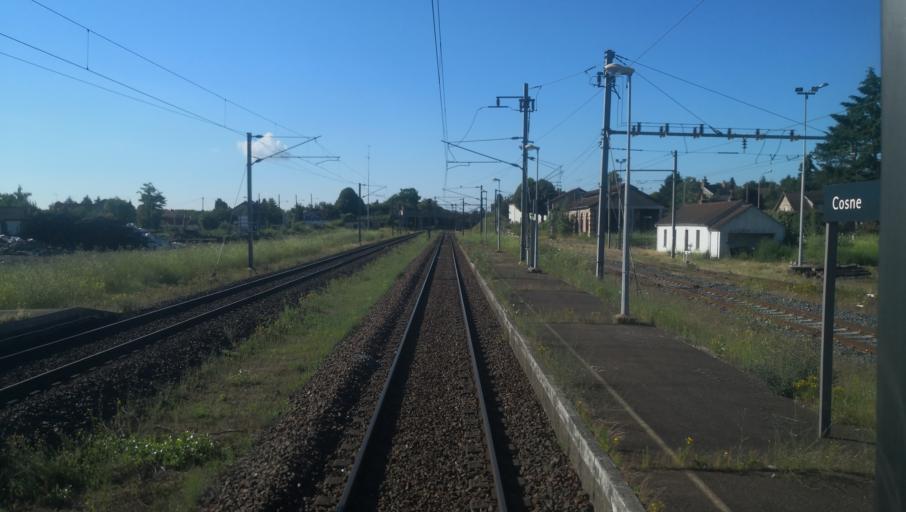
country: FR
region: Bourgogne
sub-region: Departement de la Nievre
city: Cosne-Cours-sur-Loire
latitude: 47.4158
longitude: 2.9314
